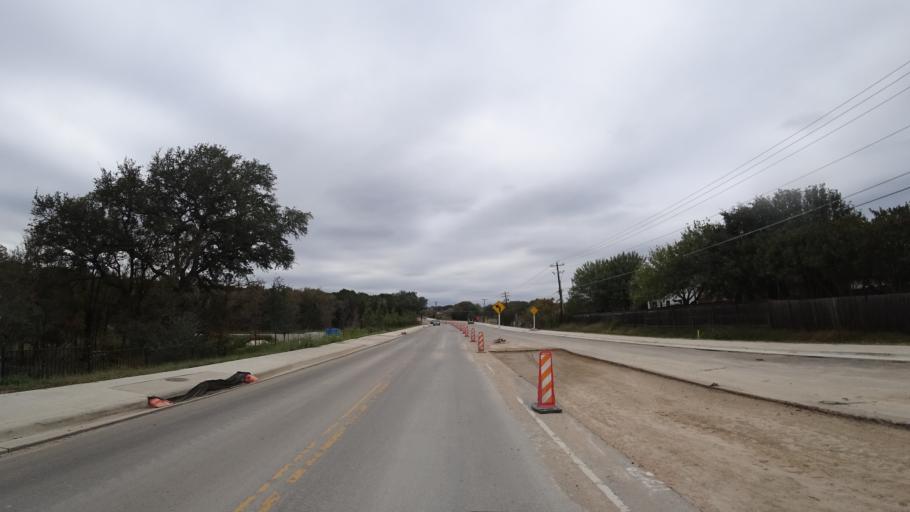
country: US
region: Texas
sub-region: Travis County
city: Manchaca
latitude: 30.1493
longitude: -97.8504
